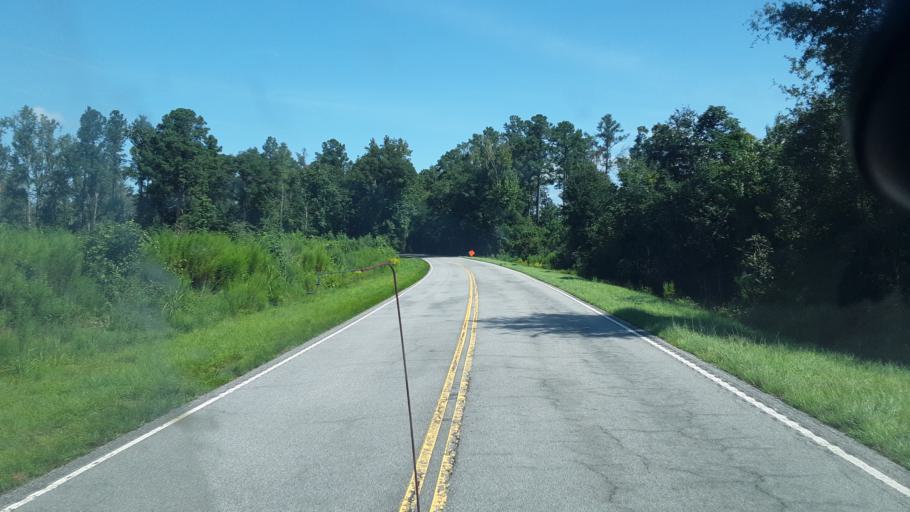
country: US
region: South Carolina
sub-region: Hampton County
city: Hampton
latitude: 32.9655
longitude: -81.0477
